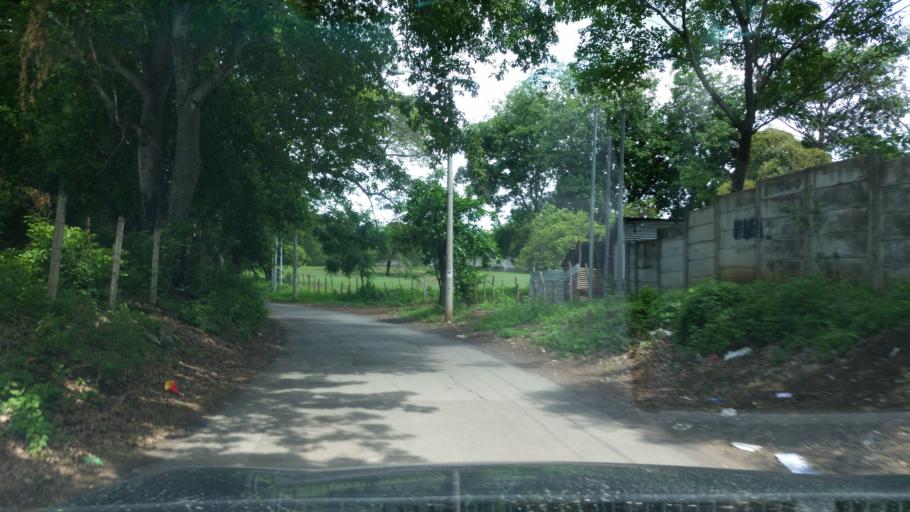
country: NI
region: Managua
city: Managua
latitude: 12.0903
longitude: -86.2227
